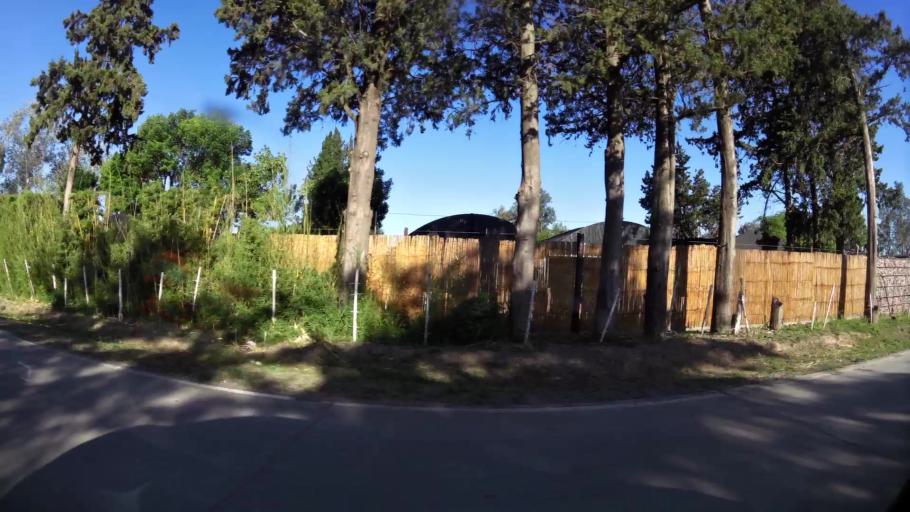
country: AR
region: Cordoba
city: San Francisco
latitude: -31.4507
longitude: -62.1019
